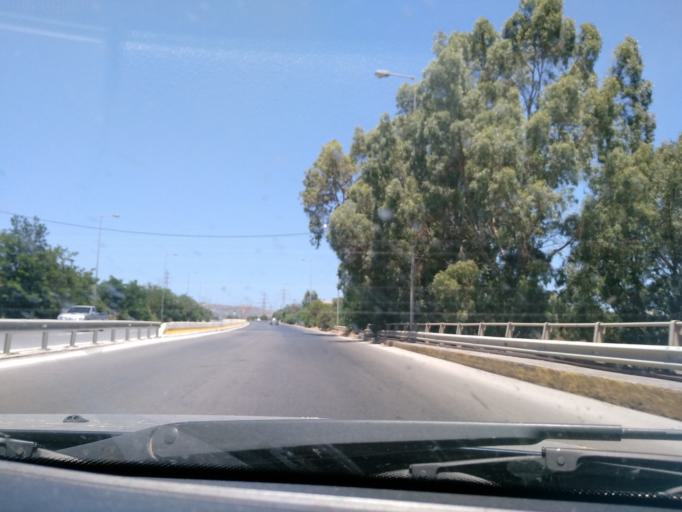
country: GR
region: Crete
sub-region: Nomos Irakleiou
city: Gazi
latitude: 35.3342
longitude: 25.0519
